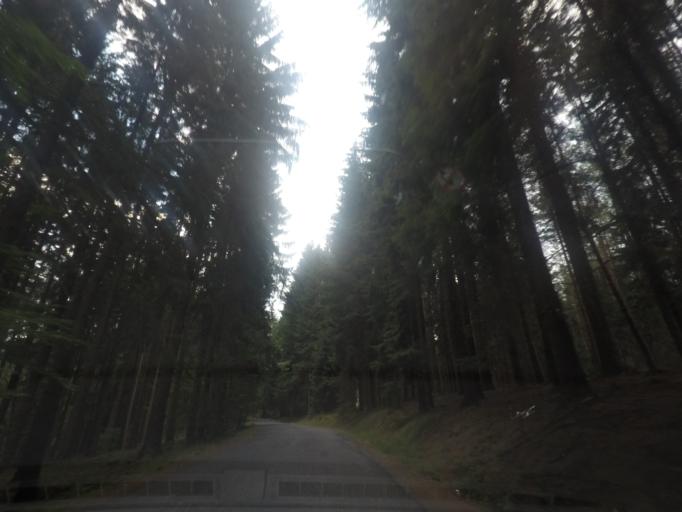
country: CZ
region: Ustecky
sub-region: Okres Decin
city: Chribska
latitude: 50.8602
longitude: 14.4433
